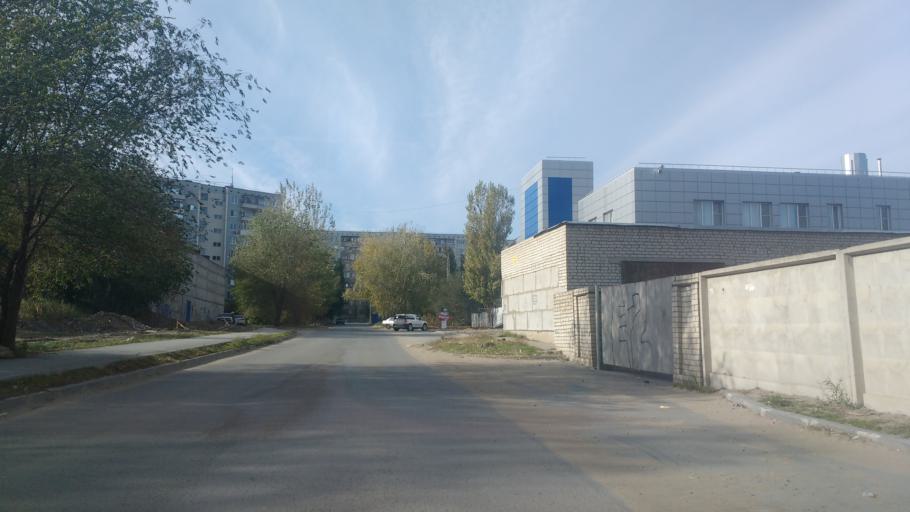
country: RU
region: Volgograd
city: Krasnoslobodsk
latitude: 48.7647
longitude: 44.5496
